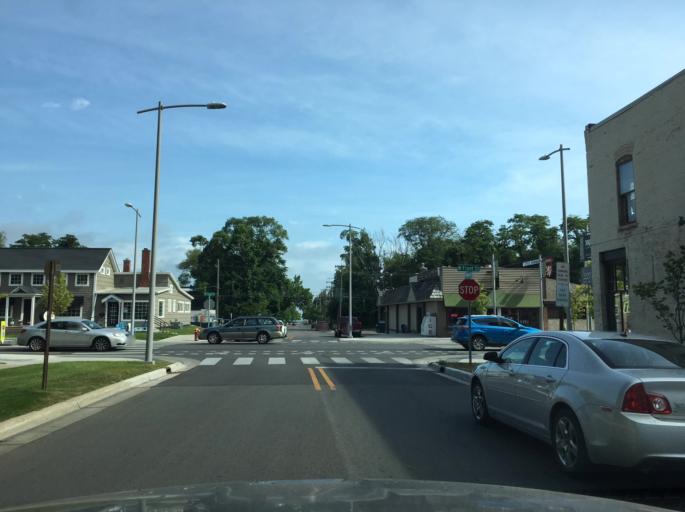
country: US
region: Michigan
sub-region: Grand Traverse County
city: Traverse City
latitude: 44.7638
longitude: -85.6330
